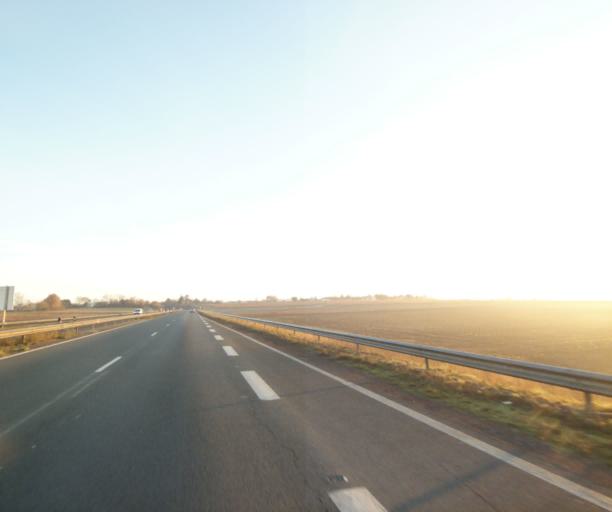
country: FR
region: Poitou-Charentes
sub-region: Departement de la Charente-Maritime
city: Les Gonds
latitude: 45.7354
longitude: -0.6078
